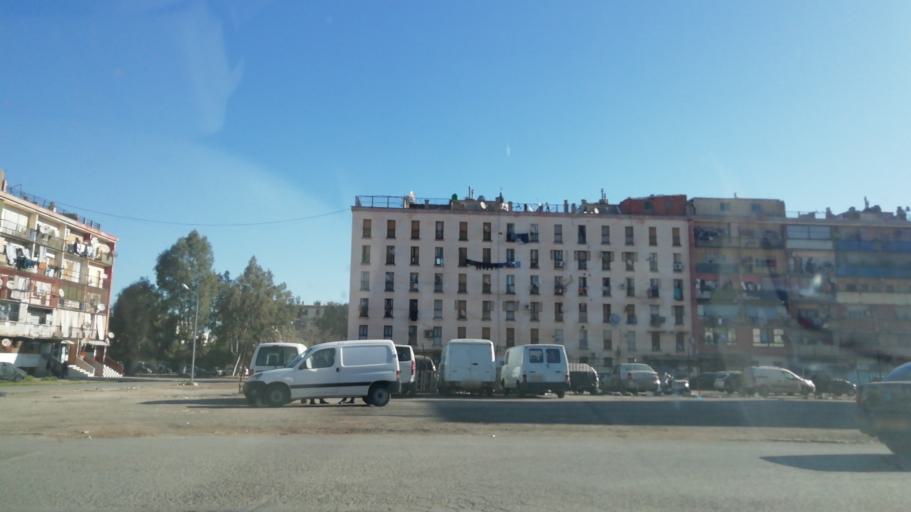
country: DZ
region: Oran
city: Oran
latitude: 35.6683
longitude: -0.6462
